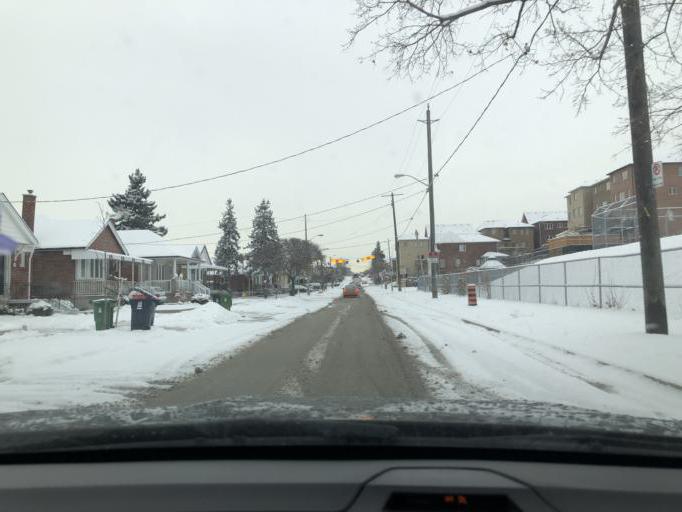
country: CA
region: Ontario
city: Toronto
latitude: 43.6866
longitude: -79.4709
